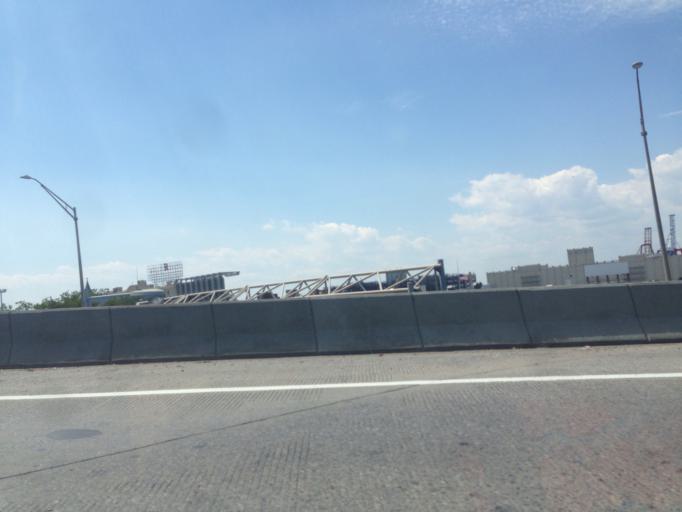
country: US
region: New York
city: New York City
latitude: 40.6800
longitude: -74.0035
